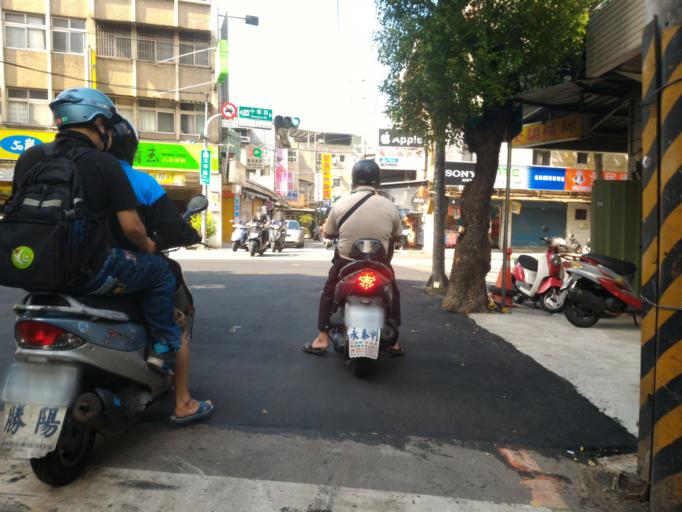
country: TW
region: Taipei
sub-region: Taipei
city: Banqiao
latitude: 24.9810
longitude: 121.4192
